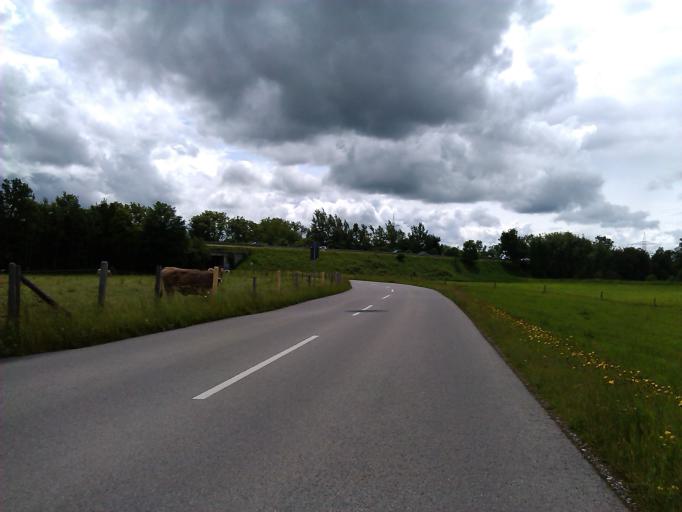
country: DE
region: Bavaria
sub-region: Swabia
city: Marktoberdorf
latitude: 47.8029
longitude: 10.6227
